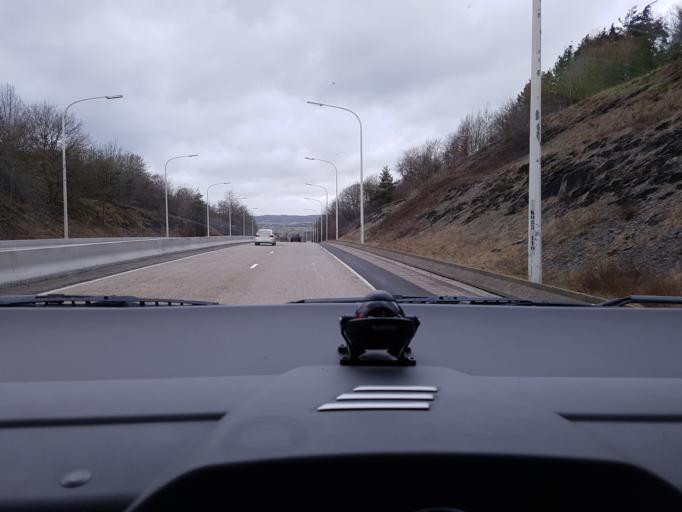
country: BE
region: Wallonia
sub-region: Province du Luxembourg
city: Marche-en-Famenne
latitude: 50.2589
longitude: 5.2640
